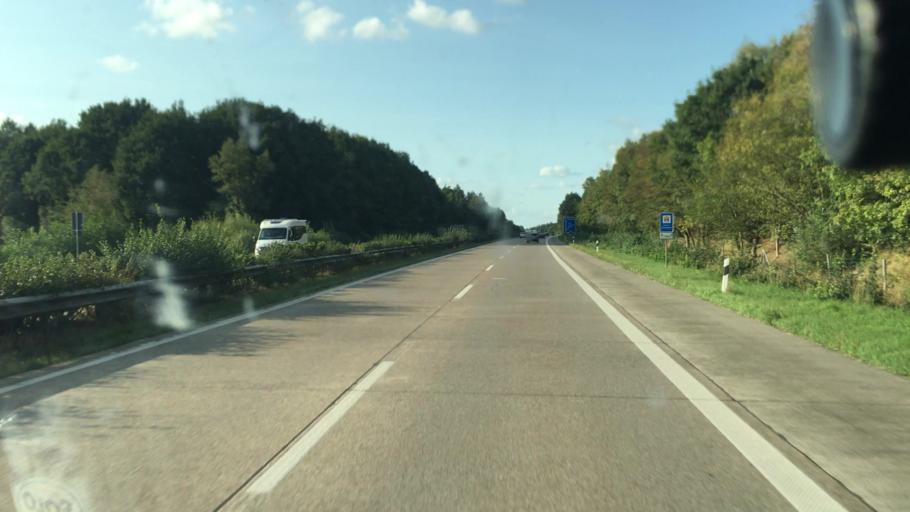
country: DE
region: Lower Saxony
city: Rastede
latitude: 53.2694
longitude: 8.1617
